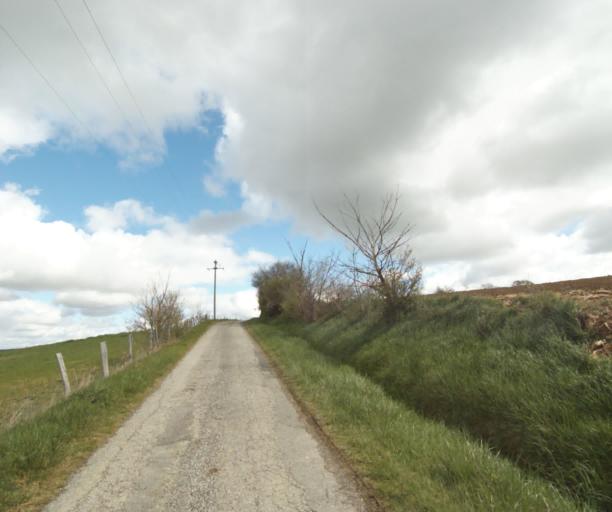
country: FR
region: Midi-Pyrenees
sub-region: Departement de l'Ariege
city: Saverdun
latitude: 43.1945
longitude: 1.5475
